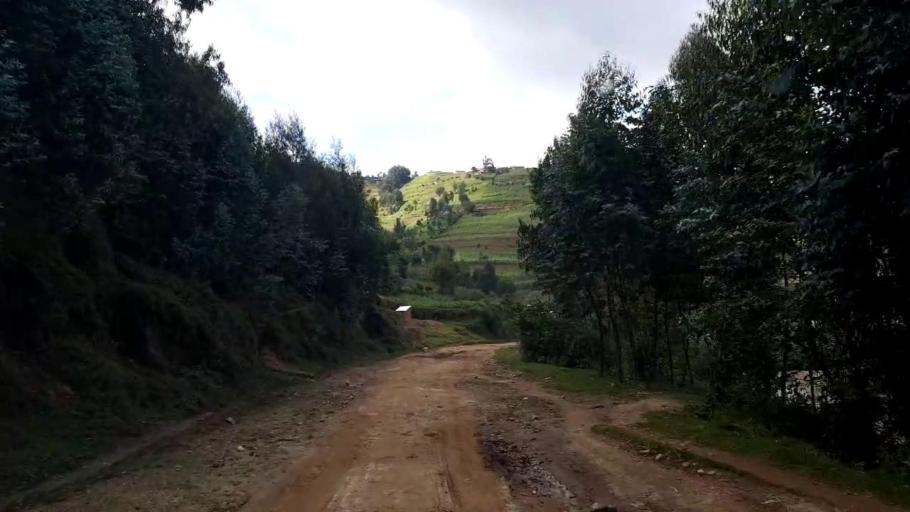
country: RW
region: Western Province
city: Kibuye
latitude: -1.8906
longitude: 29.4660
